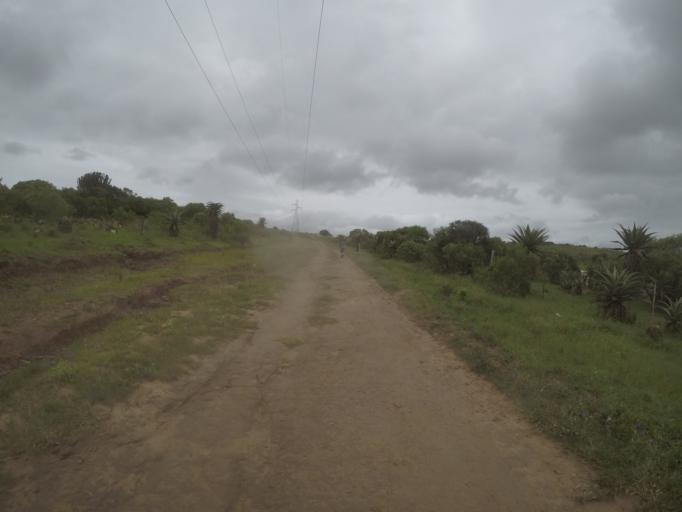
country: ZA
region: KwaZulu-Natal
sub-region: uThungulu District Municipality
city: Empangeni
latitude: -28.5979
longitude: 31.8448
